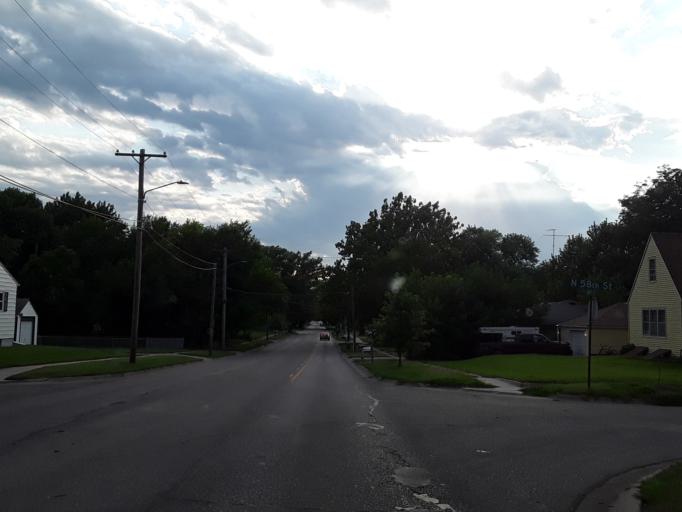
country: US
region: Nebraska
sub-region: Lancaster County
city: Lincoln
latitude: 40.8426
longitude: -96.6412
